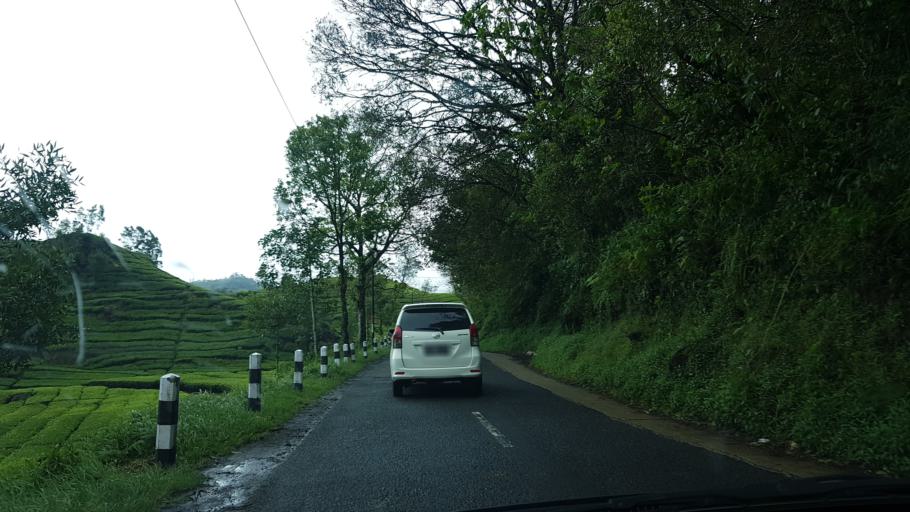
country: ID
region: West Java
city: Banjar
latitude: -7.1483
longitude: 107.3824
